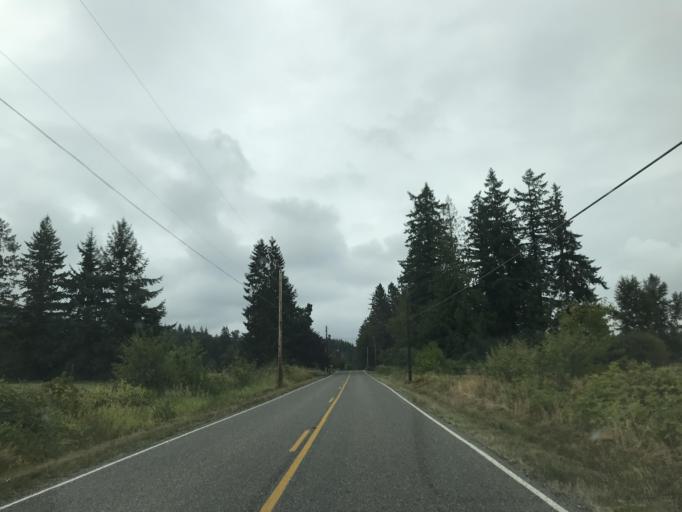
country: US
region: Washington
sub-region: Whatcom County
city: Sudden Valley
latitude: 48.7939
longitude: -122.3330
